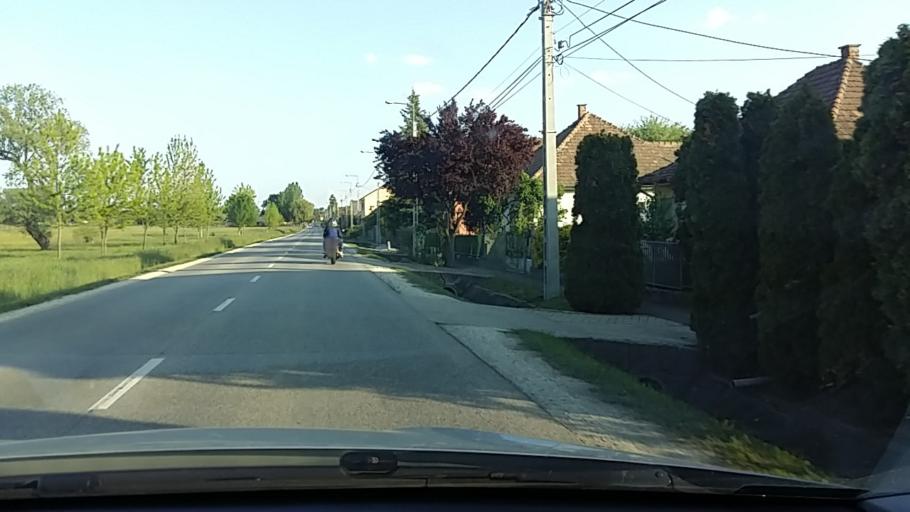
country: HU
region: Pest
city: Orbottyan
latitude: 47.7174
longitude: 19.2318
